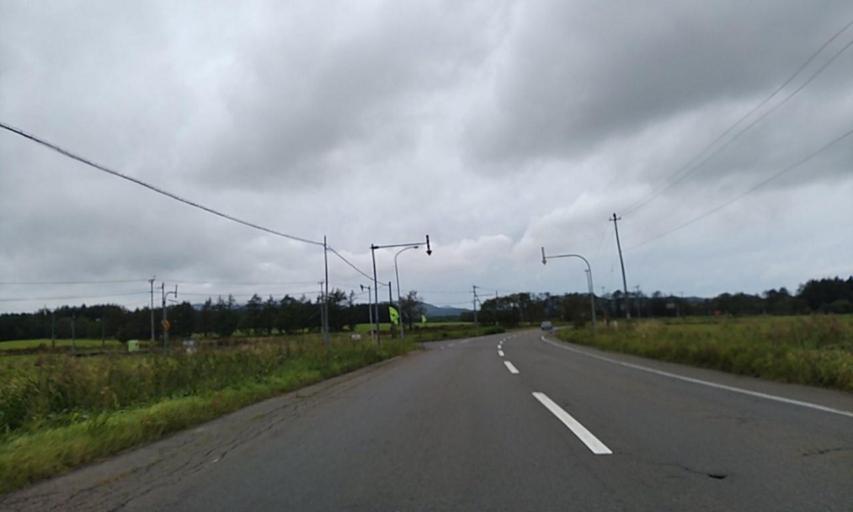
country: JP
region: Hokkaido
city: Bihoro
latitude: 43.5194
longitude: 144.4156
